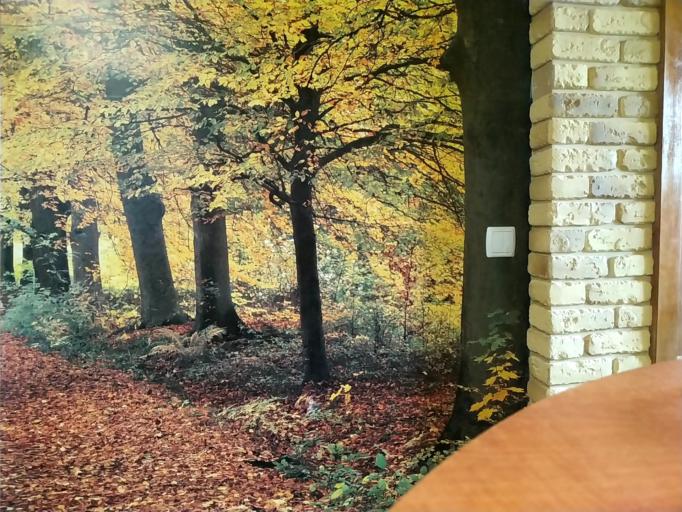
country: RU
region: Novgorod
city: Opechenskiy Posad
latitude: 58.2657
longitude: 34.0336
